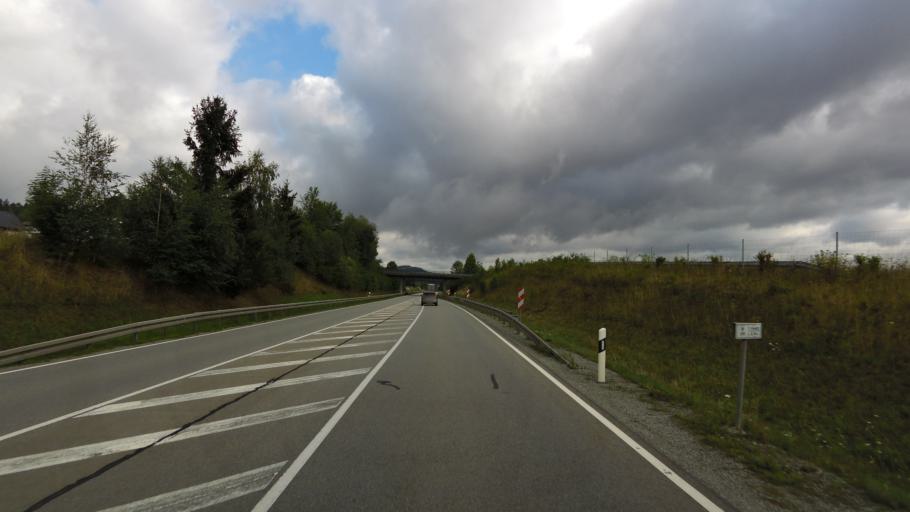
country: DE
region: Bavaria
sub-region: Lower Bavaria
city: Ascha
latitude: 48.9907
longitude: 12.6308
